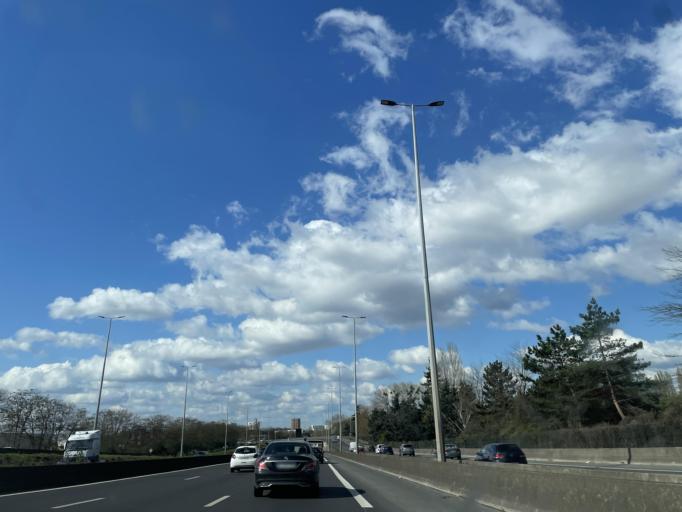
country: FR
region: Ile-de-France
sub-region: Departement de Seine-Saint-Denis
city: La Courneuve
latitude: 48.9389
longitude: 2.4076
